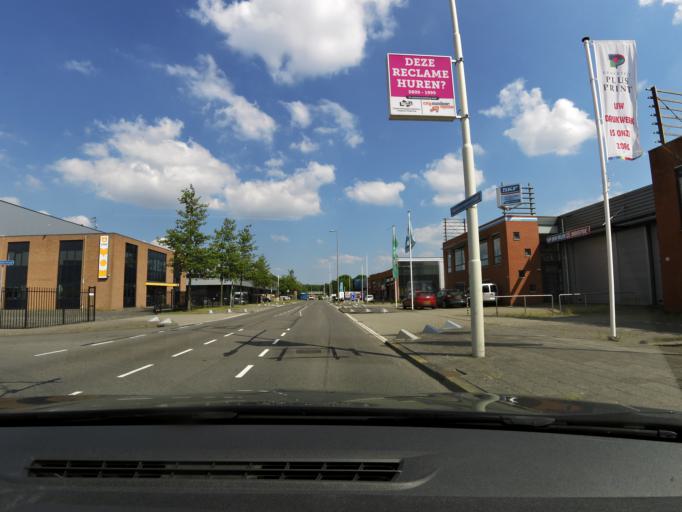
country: NL
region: South Holland
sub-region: Gemeente Albrandswaard
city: Rhoon
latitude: 51.8674
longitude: 4.3768
